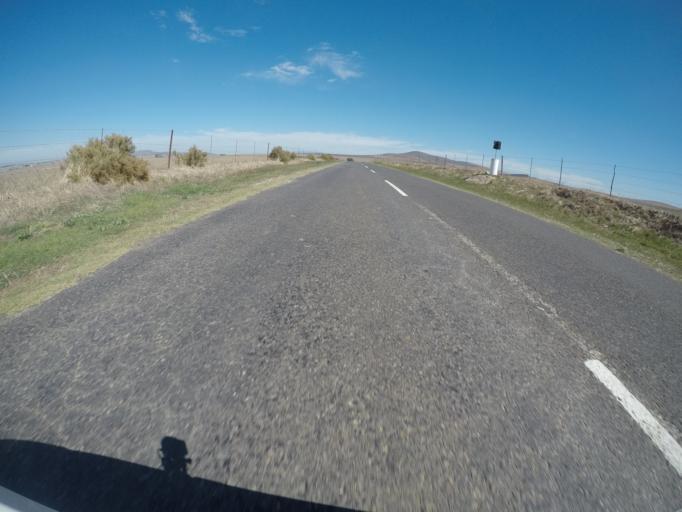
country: ZA
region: Western Cape
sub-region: City of Cape Town
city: Atlantis
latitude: -33.6847
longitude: 18.6000
